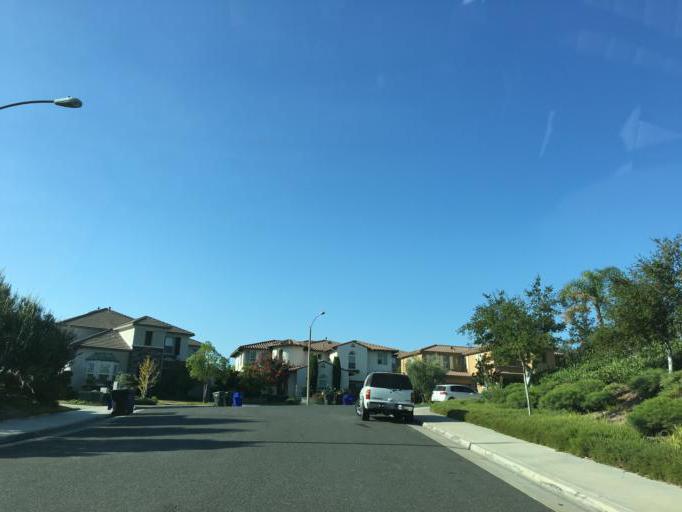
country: US
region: California
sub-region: Los Angeles County
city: Valencia
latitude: 34.4093
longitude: -118.5900
